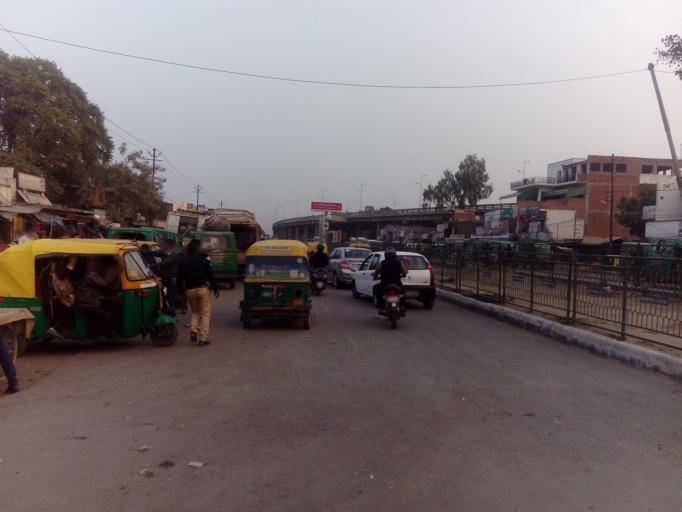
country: IN
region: Uttar Pradesh
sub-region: Kanpur
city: Kanpur
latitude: 26.4109
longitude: 80.3876
